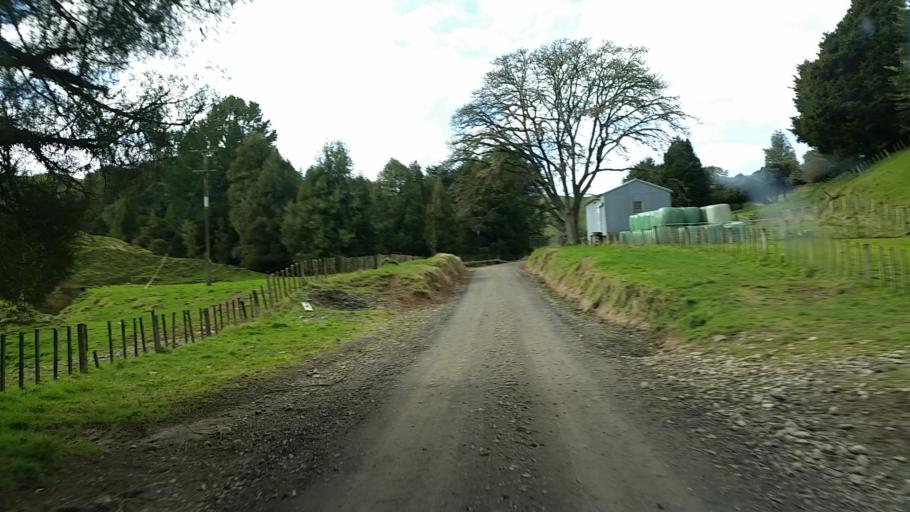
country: NZ
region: Taranaki
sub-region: New Plymouth District
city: Waitara
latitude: -39.1617
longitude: 174.5852
